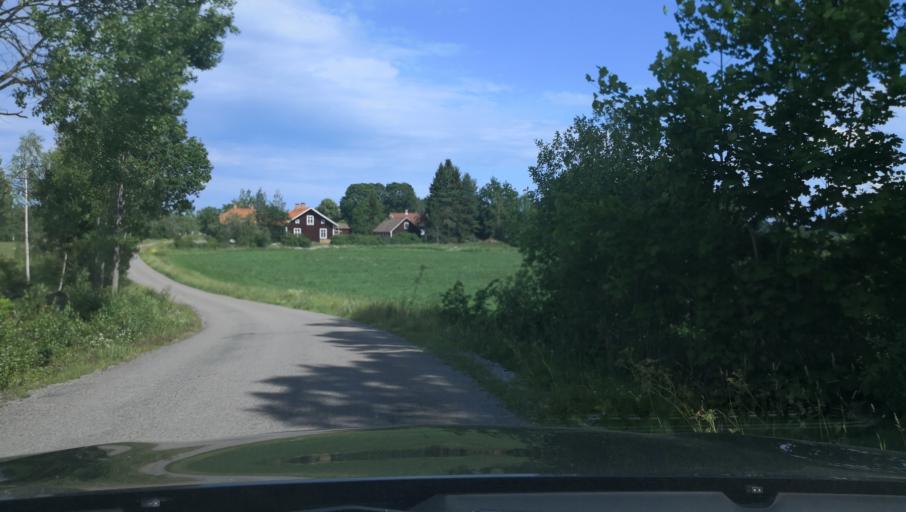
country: SE
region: Vaestmanland
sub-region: Surahammars Kommun
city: Ramnas
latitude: 59.9478
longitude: 16.2133
